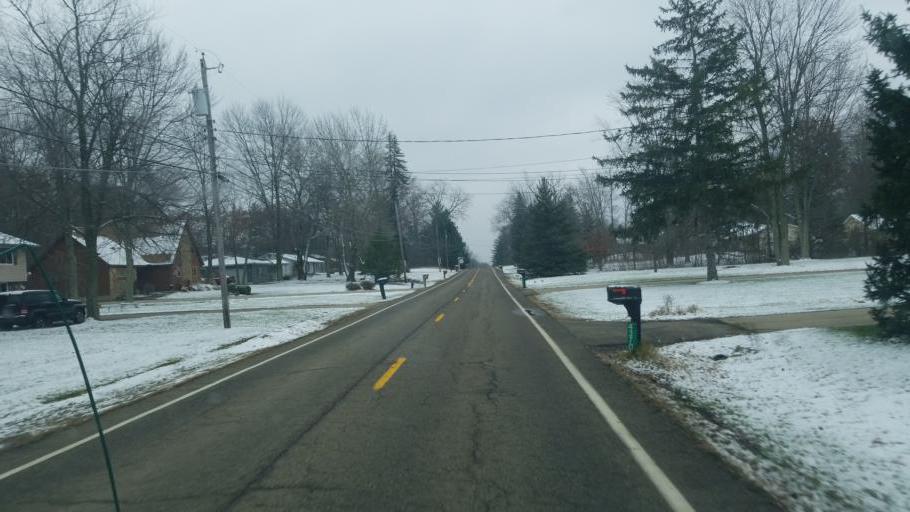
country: US
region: Ohio
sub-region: Cuyahoga County
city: Broadview Heights
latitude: 41.2772
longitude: -81.6724
